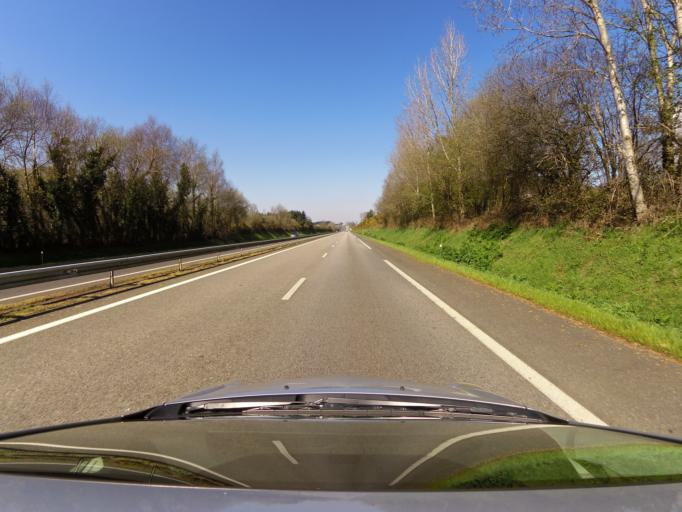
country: FR
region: Brittany
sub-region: Departement du Morbihan
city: Josselin
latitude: 47.9444
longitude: -2.5093
